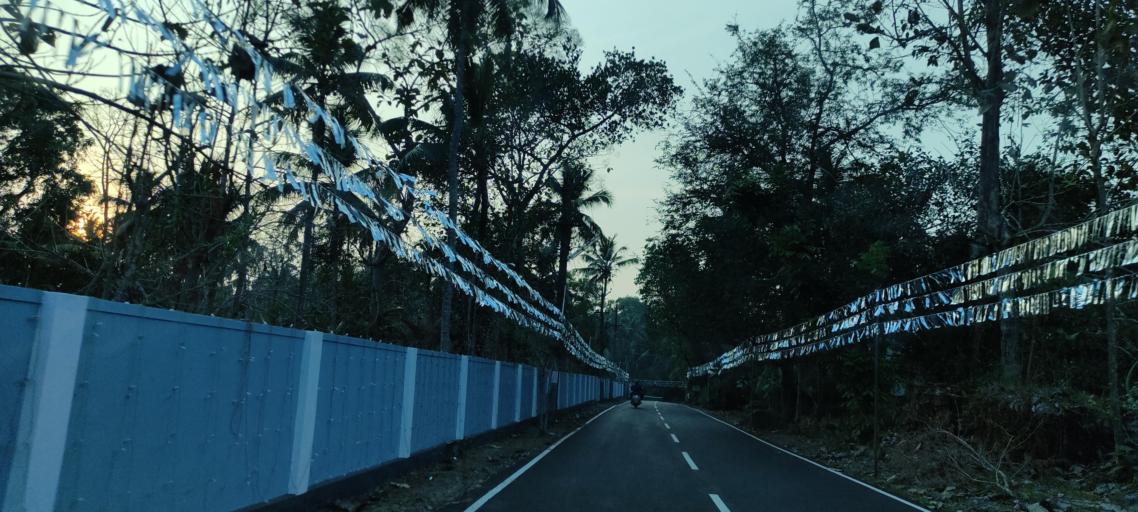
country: IN
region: Kerala
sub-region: Alappuzha
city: Mavelikara
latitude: 9.2680
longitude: 76.5477
